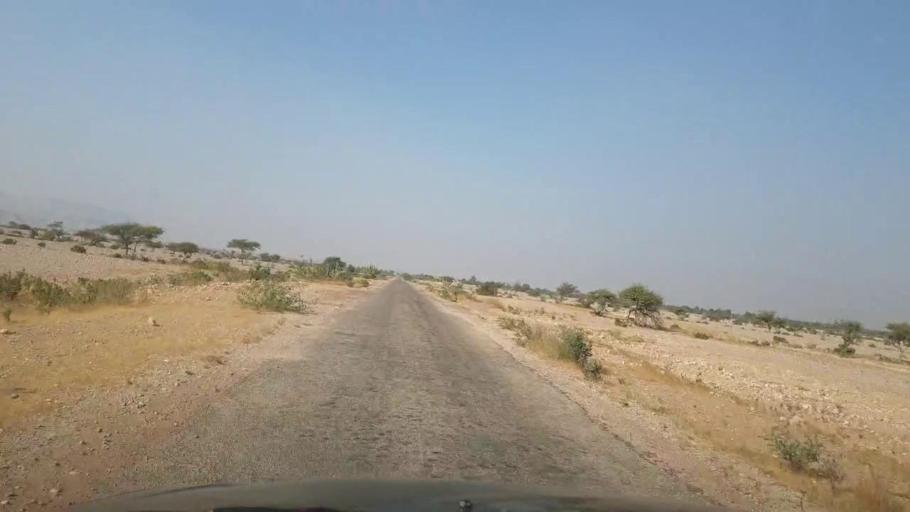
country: PK
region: Sindh
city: Jamshoro
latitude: 25.5805
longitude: 67.8215
